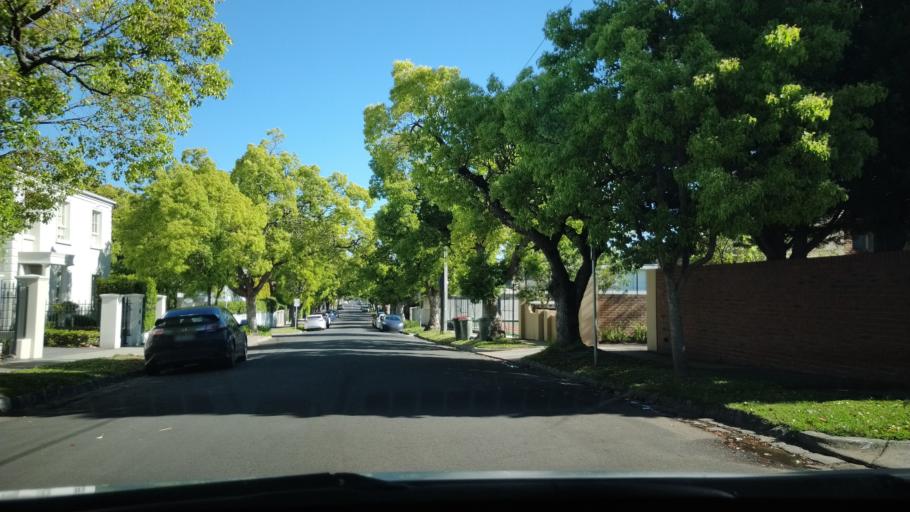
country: AU
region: Victoria
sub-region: Bayside
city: Brighton East
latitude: -37.9025
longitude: 145.0175
